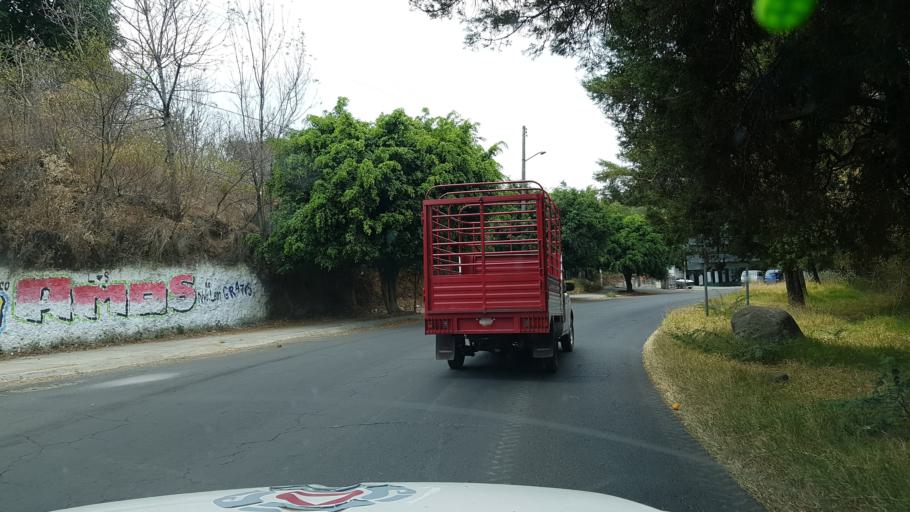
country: MX
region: Morelos
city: Ocuituco
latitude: 18.8781
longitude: -98.7800
